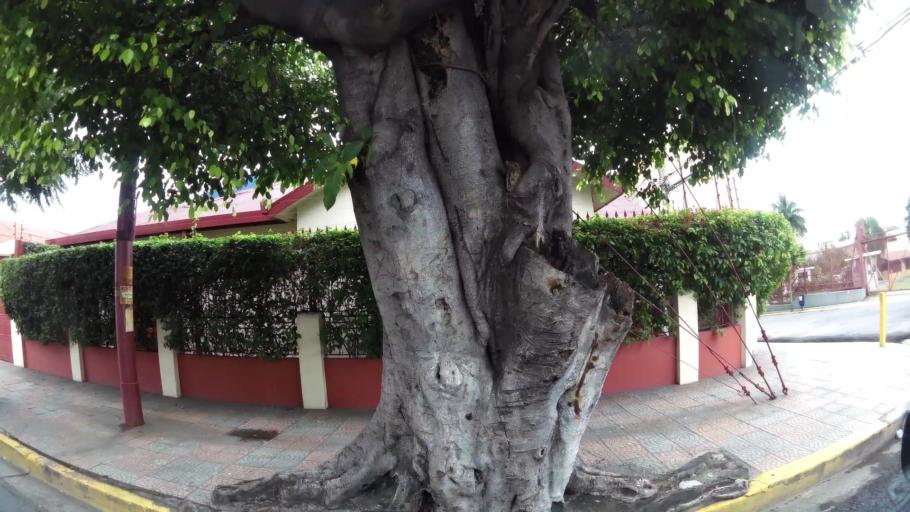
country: CR
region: San Jose
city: San Jose
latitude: 9.9320
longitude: -84.0883
